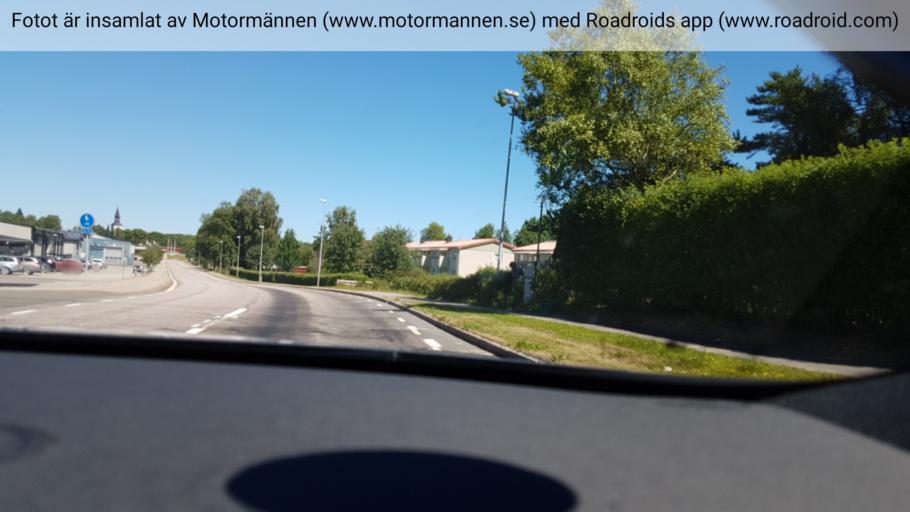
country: SE
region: Vaestra Goetaland
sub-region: Ulricehamns Kommun
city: Ulricehamn
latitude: 57.9209
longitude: 13.4890
